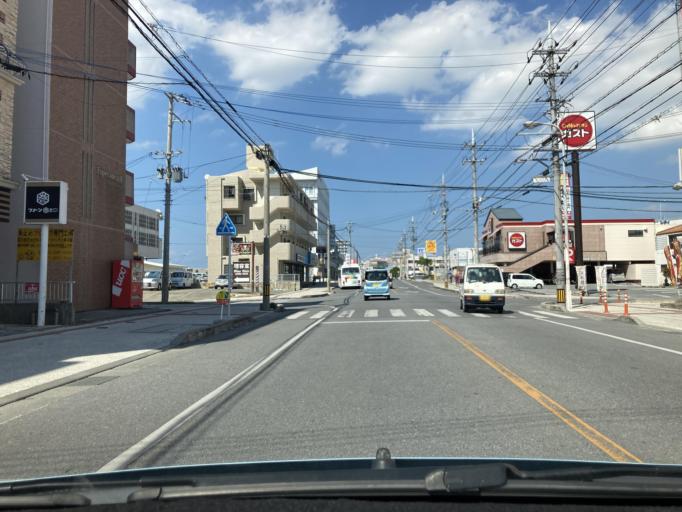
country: JP
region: Okinawa
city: Tomigusuku
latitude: 26.1890
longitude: 127.7093
